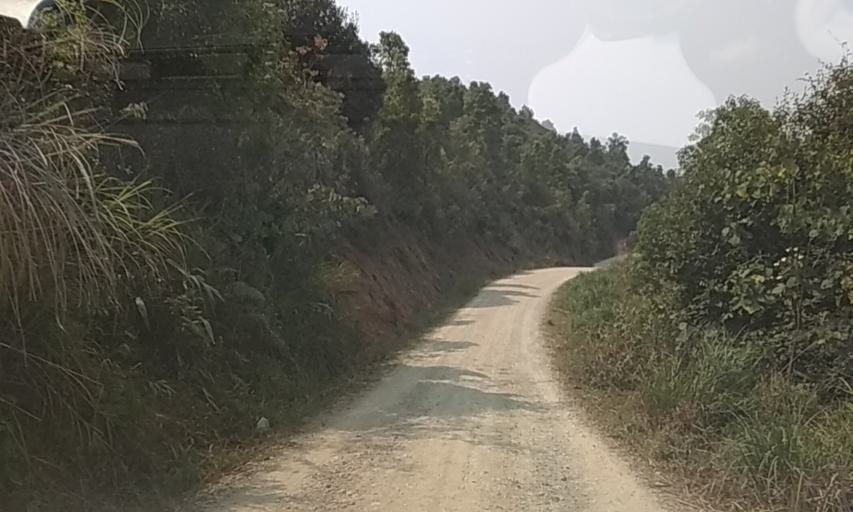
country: TH
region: Nan
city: Chaloem Phra Kiat
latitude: 20.0515
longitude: 101.0724
